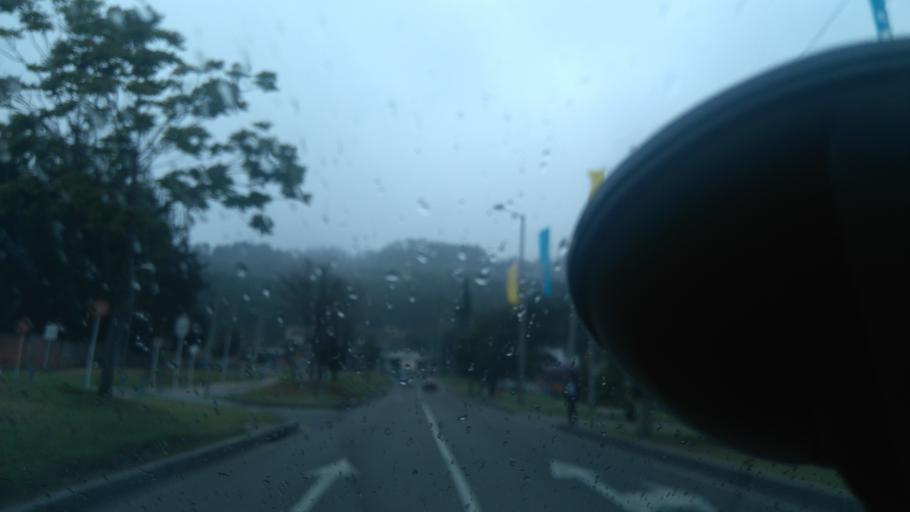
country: CO
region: Cundinamarca
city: La Calera
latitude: 4.7471
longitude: -74.0249
